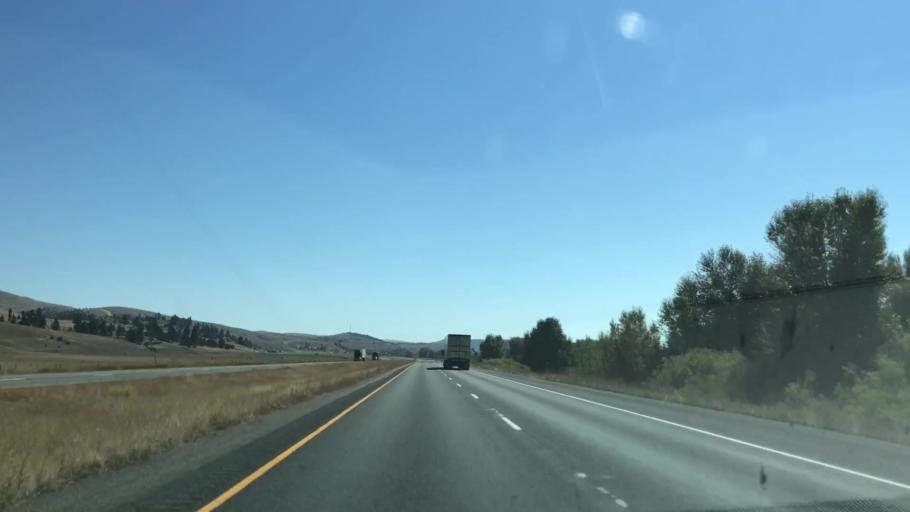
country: US
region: Montana
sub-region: Powell County
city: Deer Lodge
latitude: 46.6061
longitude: -112.9692
